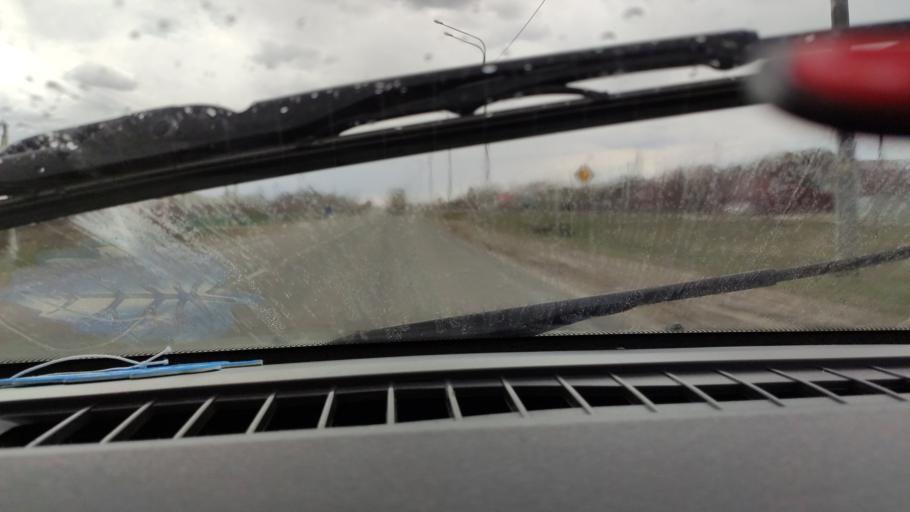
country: RU
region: Saratov
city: Sinodskoye
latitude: 51.9898
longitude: 46.6674
